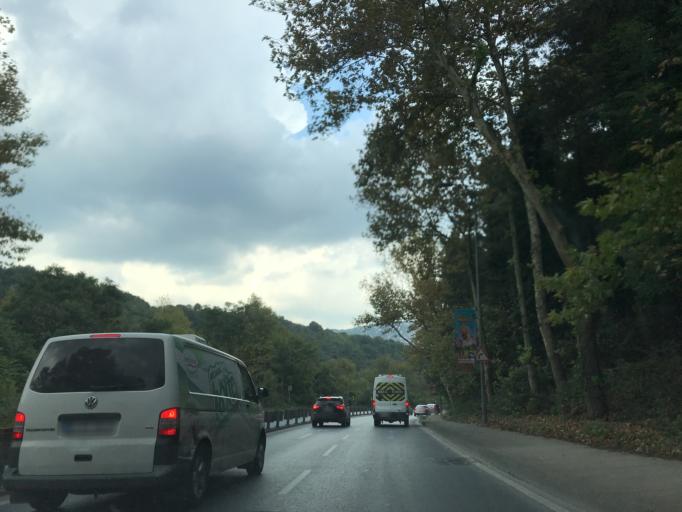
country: TR
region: Istanbul
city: Arikoey
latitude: 41.1463
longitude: 29.0279
